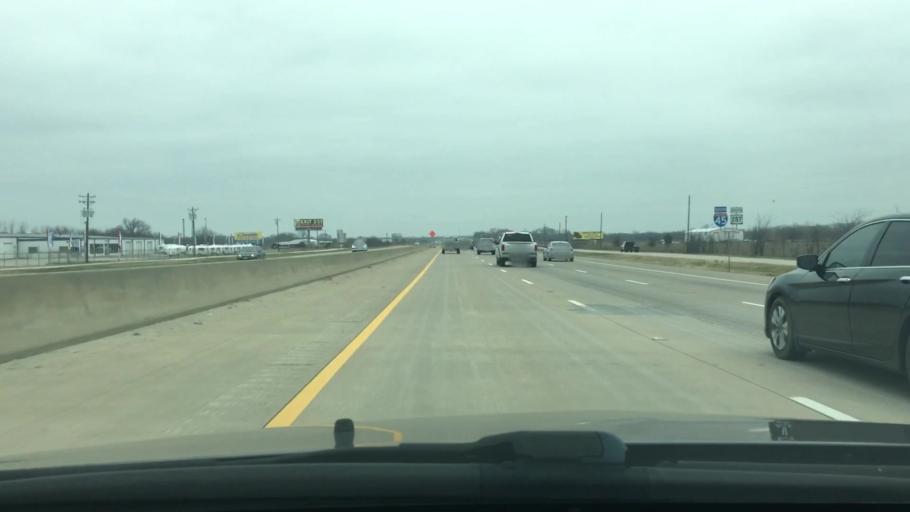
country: US
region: Texas
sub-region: Navarro County
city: Corsicana
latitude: 32.1920
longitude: -96.4729
